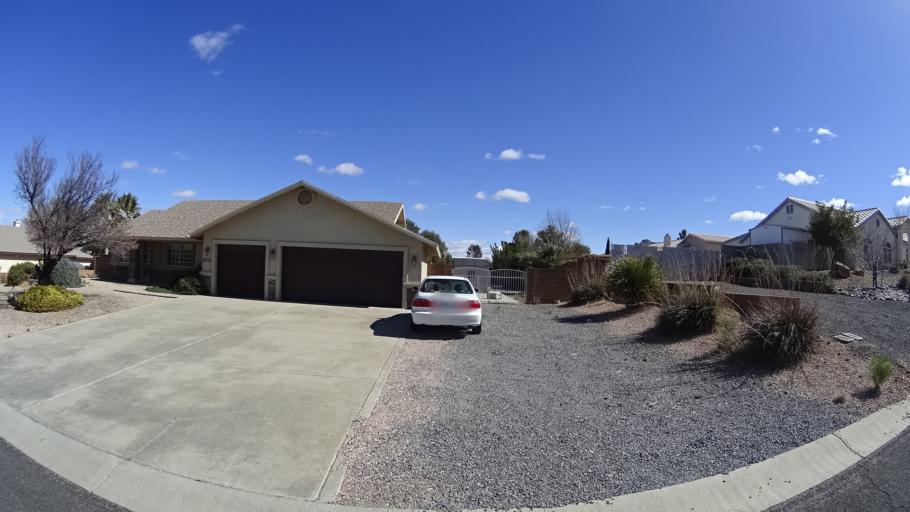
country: US
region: Arizona
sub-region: Mohave County
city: Kingman
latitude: 35.1982
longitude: -113.9634
